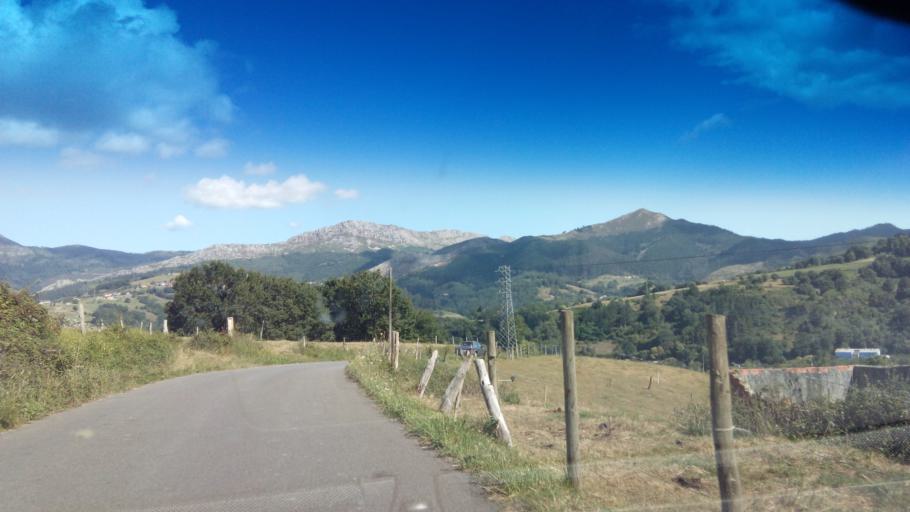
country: ES
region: Asturias
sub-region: Province of Asturias
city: Parres
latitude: 43.3781
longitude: -5.1773
